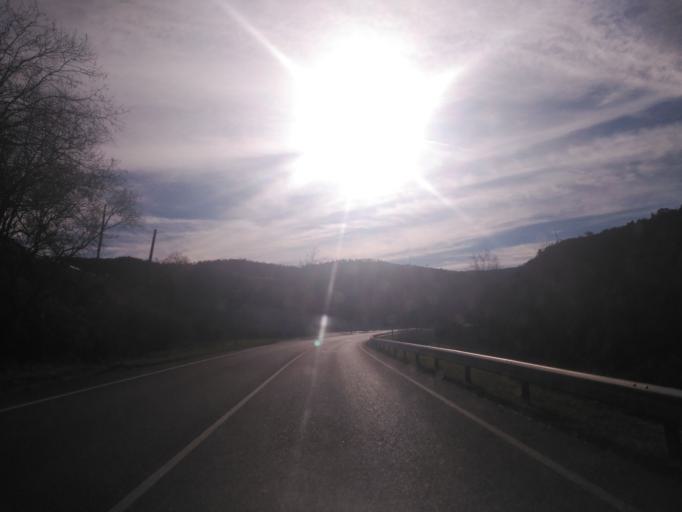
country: ES
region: Cantabria
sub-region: Provincia de Cantabria
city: Comillas
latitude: 43.3631
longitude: -4.2696
